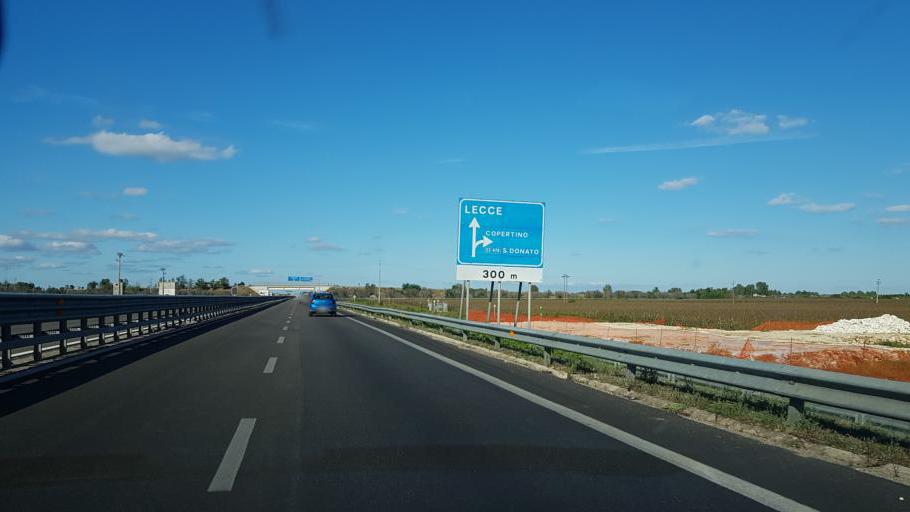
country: IT
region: Apulia
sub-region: Provincia di Lecce
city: Collemeto
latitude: 40.2536
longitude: 18.1169
